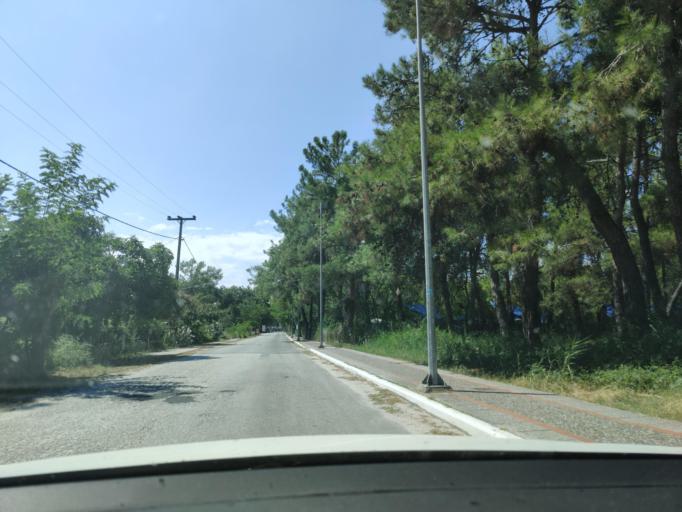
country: GR
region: East Macedonia and Thrace
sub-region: Nomos Kavalas
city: Prinos
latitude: 40.7602
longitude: 24.5673
